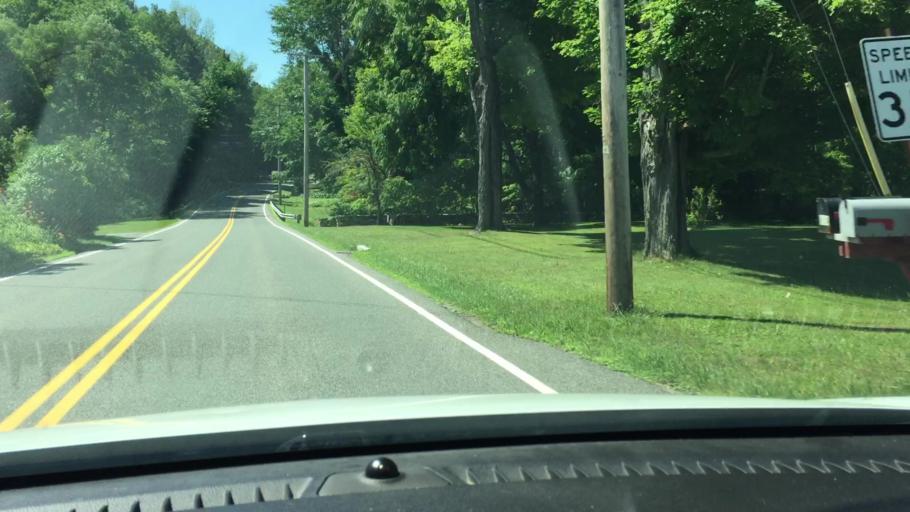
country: US
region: Massachusetts
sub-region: Berkshire County
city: Lenox
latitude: 42.3817
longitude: -73.2566
